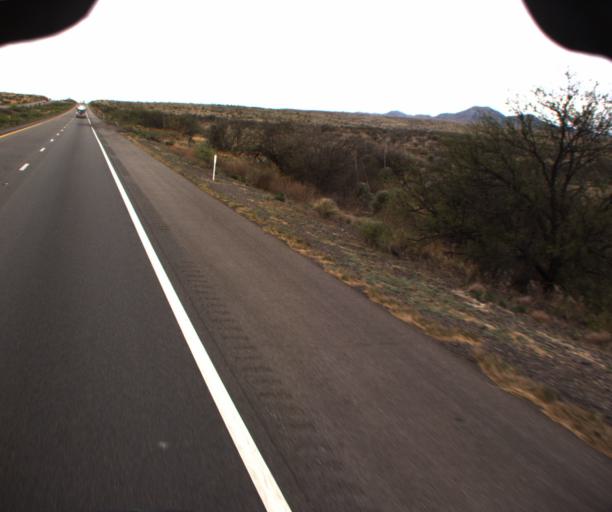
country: US
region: Arizona
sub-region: Cochise County
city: Willcox
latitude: 32.1427
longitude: -109.9998
